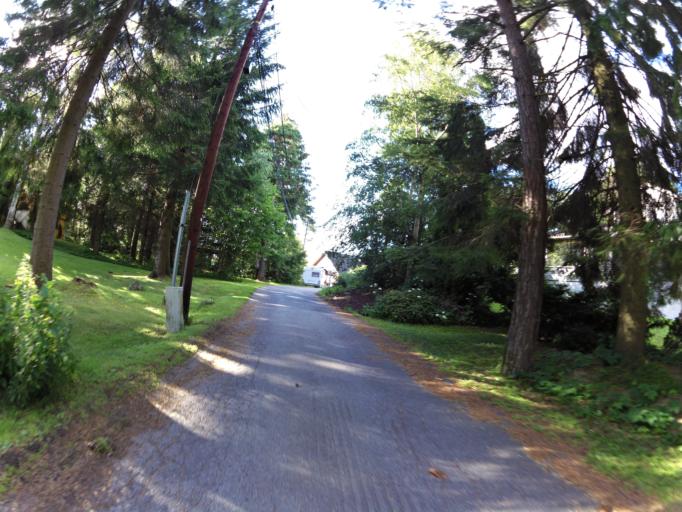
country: NO
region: Ostfold
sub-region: Fredrikstad
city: Fredrikstad
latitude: 59.2211
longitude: 10.9549
